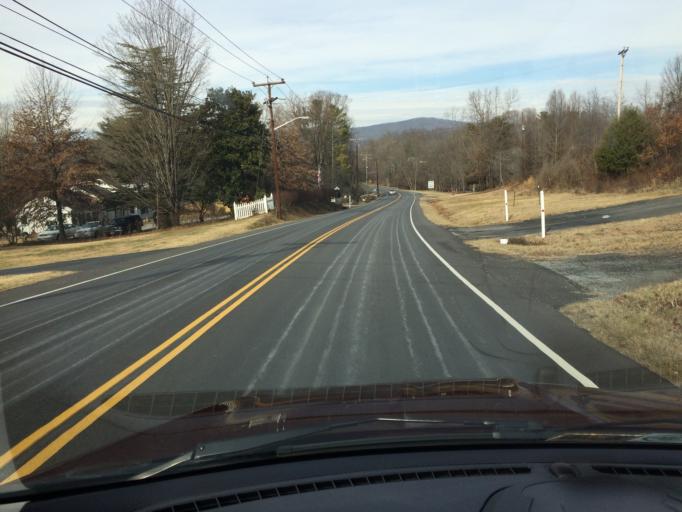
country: US
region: Virginia
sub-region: Roanoke County
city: Hollins
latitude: 37.3426
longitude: -79.9455
